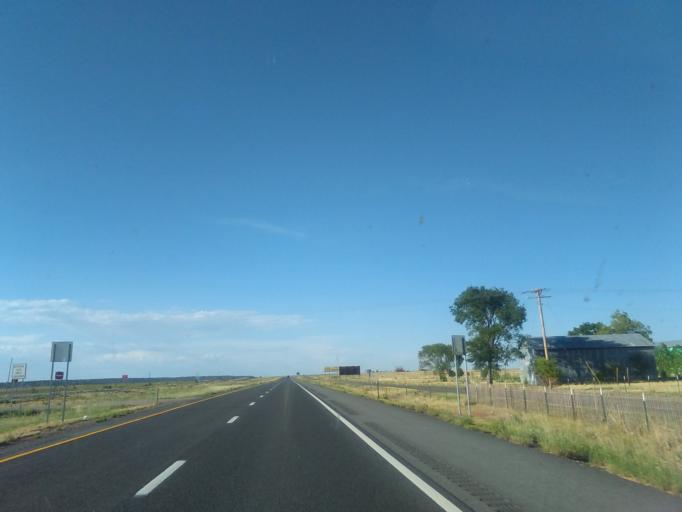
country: US
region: New Mexico
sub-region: San Miguel County
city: Las Vegas
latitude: 35.6572
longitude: -105.1886
